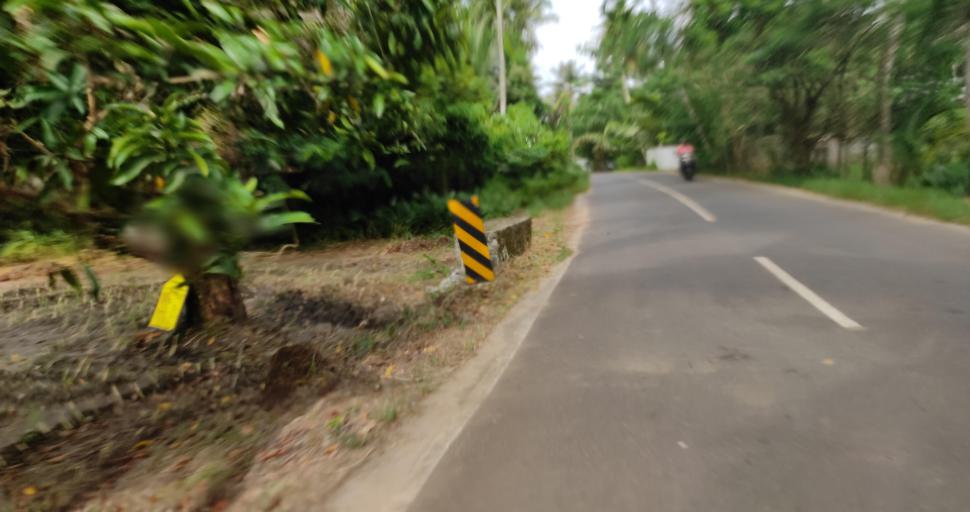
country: IN
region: Kerala
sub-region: Alappuzha
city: Vayalar
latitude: 9.6551
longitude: 76.3037
